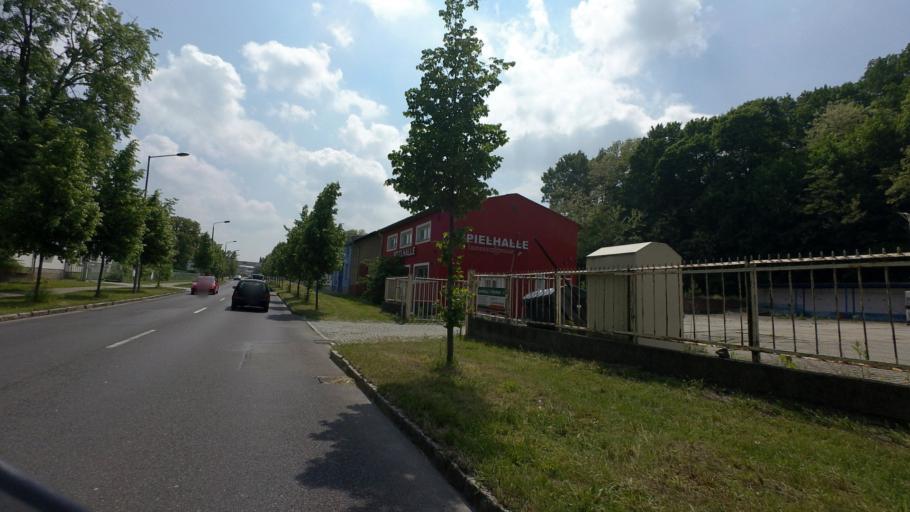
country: DE
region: Brandenburg
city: Spremberg
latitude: 51.5744
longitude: 14.3647
